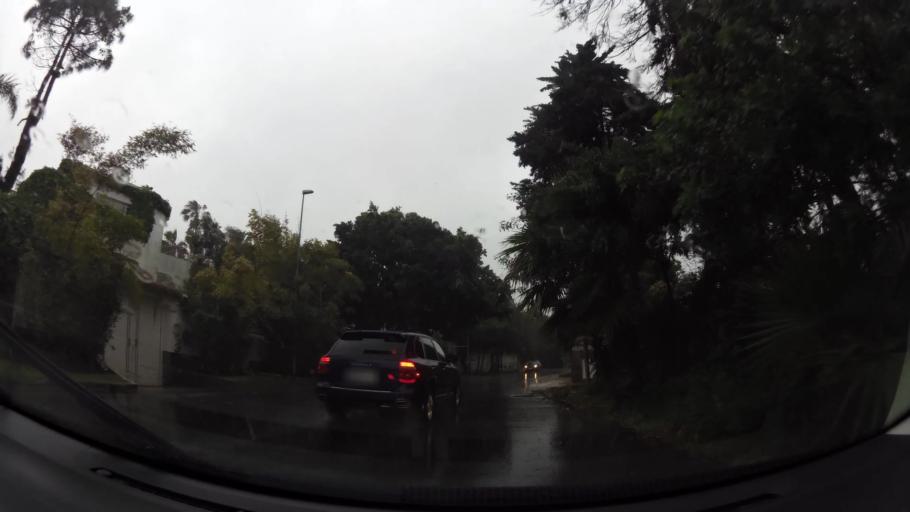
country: MA
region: Grand Casablanca
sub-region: Casablanca
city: Casablanca
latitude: 33.5904
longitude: -7.6679
